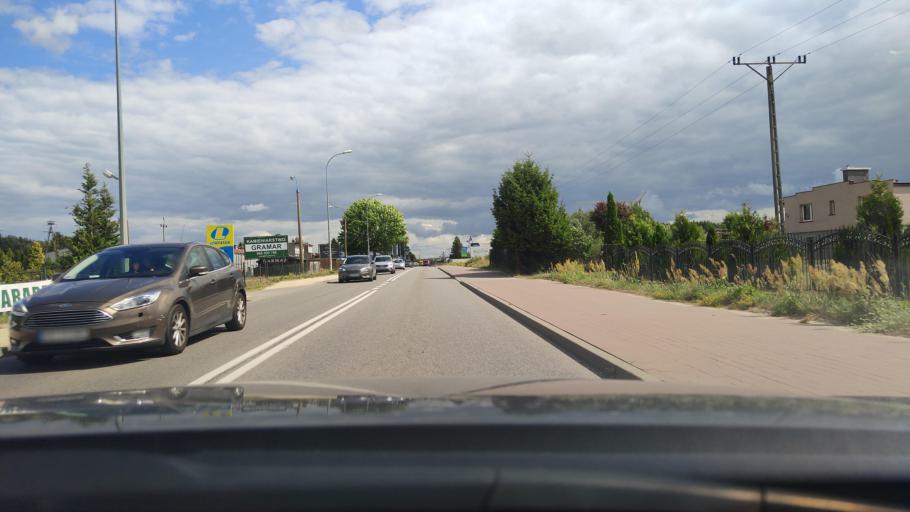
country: PL
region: Pomeranian Voivodeship
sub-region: Powiat wejherowski
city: Bojano
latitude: 54.4766
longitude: 18.3700
